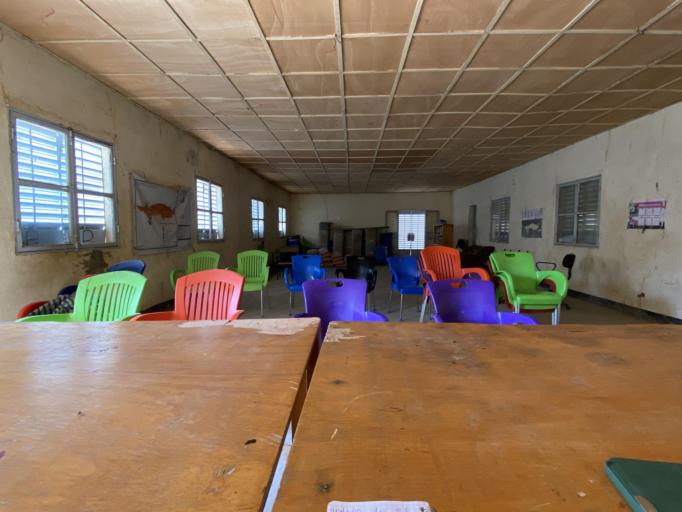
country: NE
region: Maradi
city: Tibiri
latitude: 13.5410
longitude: 6.8825
